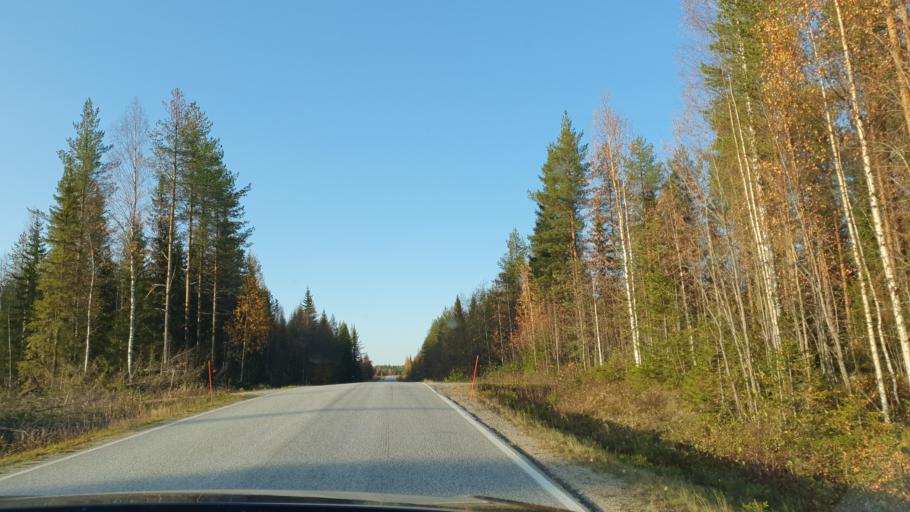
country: FI
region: Kainuu
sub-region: Kehys-Kainuu
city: Kuhmo
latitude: 64.3826
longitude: 29.4742
